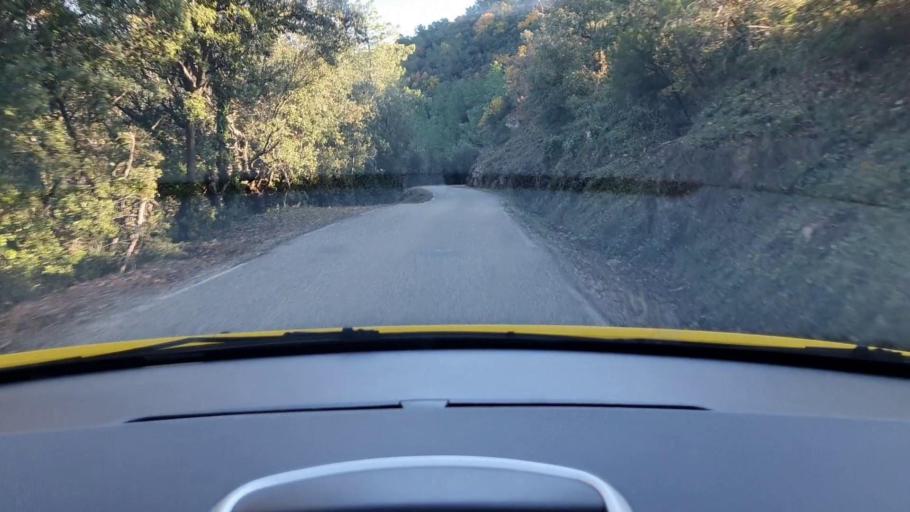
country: FR
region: Languedoc-Roussillon
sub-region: Departement du Gard
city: Branoux-les-Taillades
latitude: 44.2259
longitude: 3.9975
